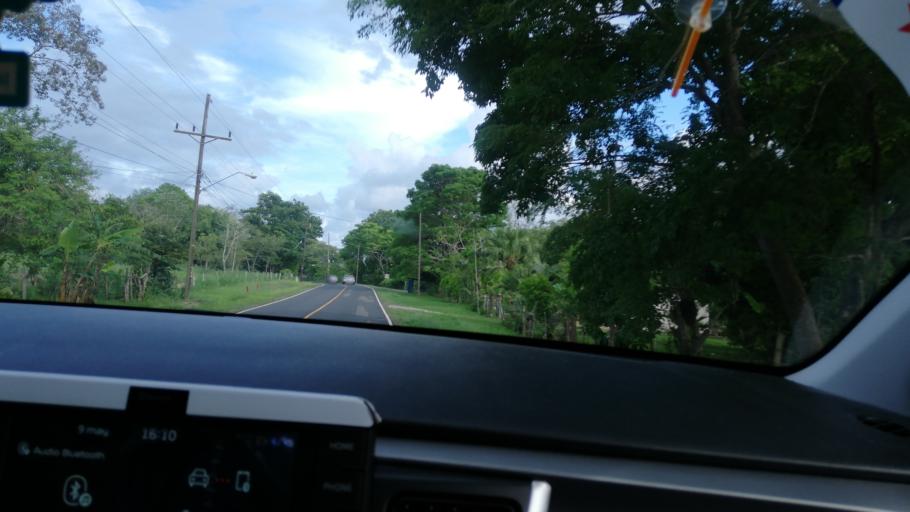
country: PA
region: Panama
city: Las Colinas
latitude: 8.4889
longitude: -80.0227
